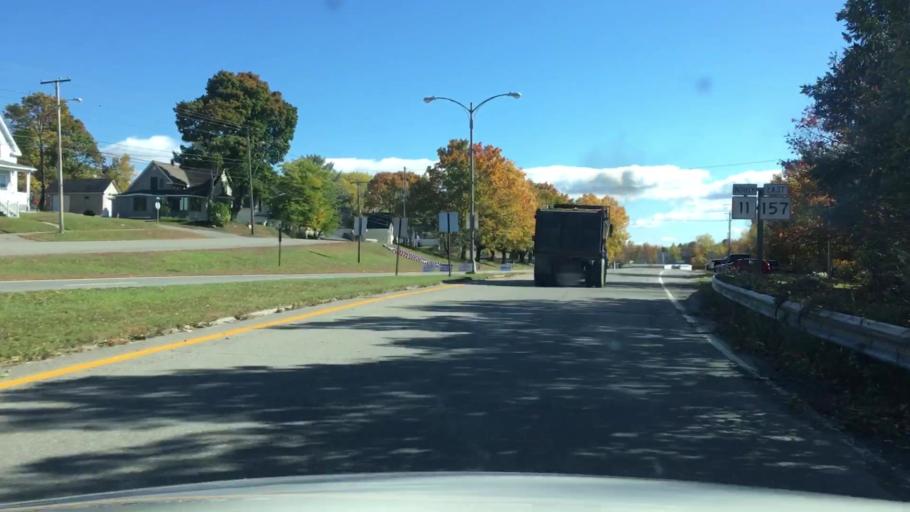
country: US
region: Maine
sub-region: Penobscot County
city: East Millinocket
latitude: 45.6248
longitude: -68.5720
